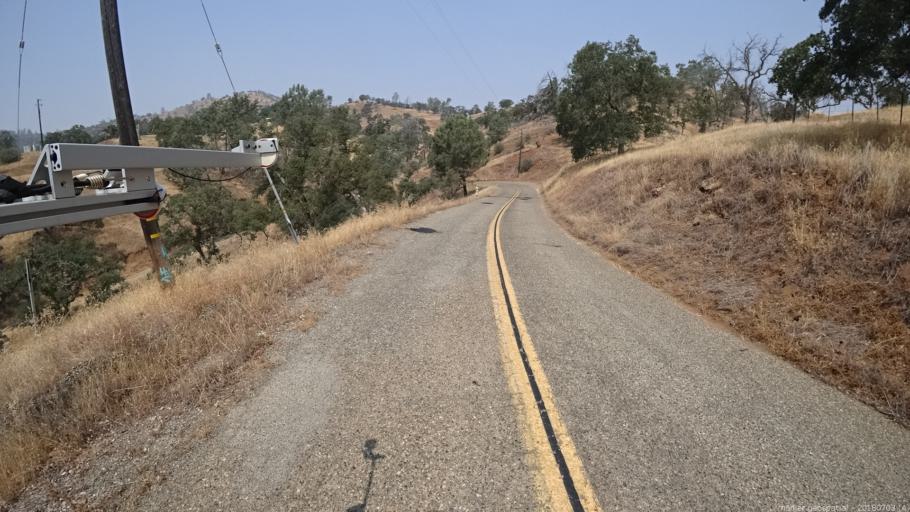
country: US
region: California
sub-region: Fresno County
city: Auberry
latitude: 37.0543
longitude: -119.6514
